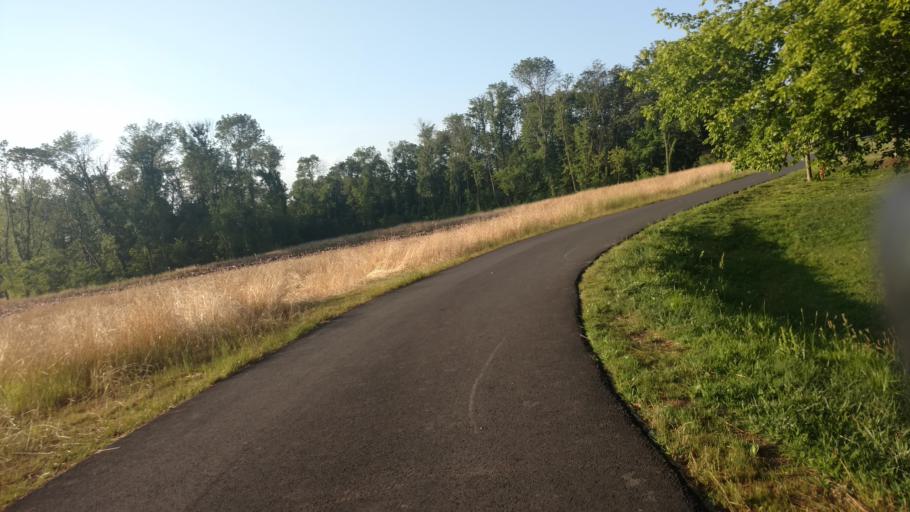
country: US
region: Virginia
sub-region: City of Alexandria
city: Alexandria
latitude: 38.8427
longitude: -77.0609
